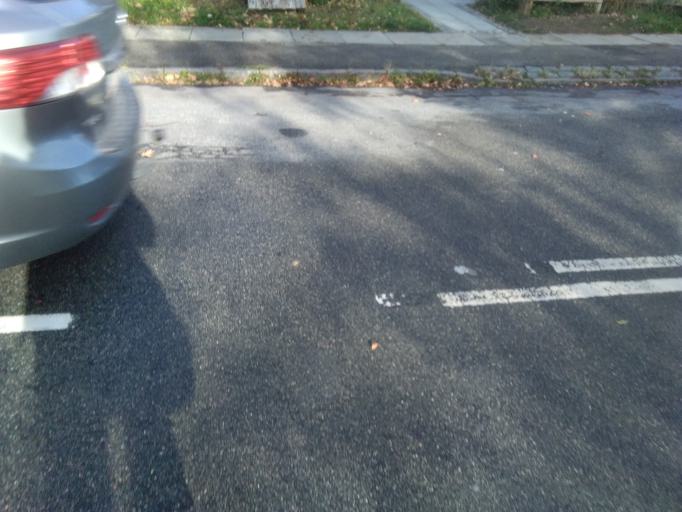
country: DK
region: Capital Region
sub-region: Kobenhavn
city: Vanlose
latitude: 55.6976
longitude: 12.4935
